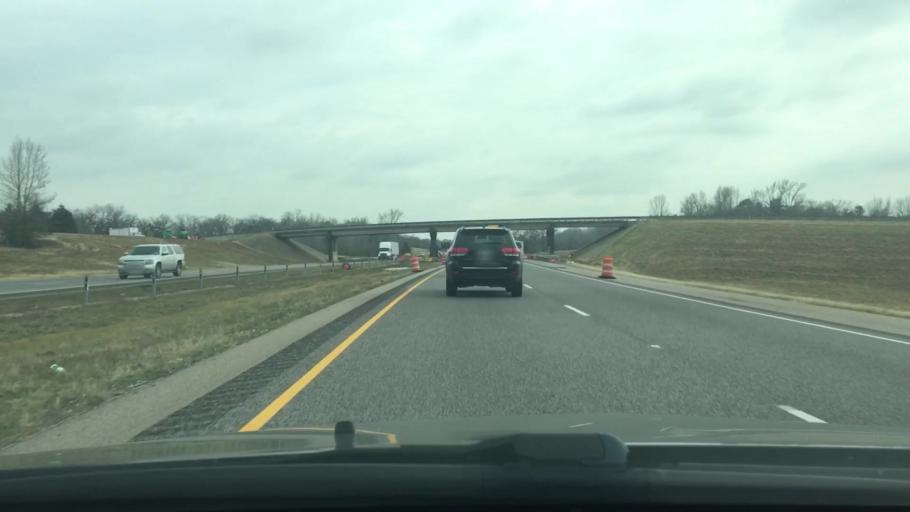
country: US
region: Texas
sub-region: Leon County
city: Buffalo
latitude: 31.5013
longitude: -96.0977
